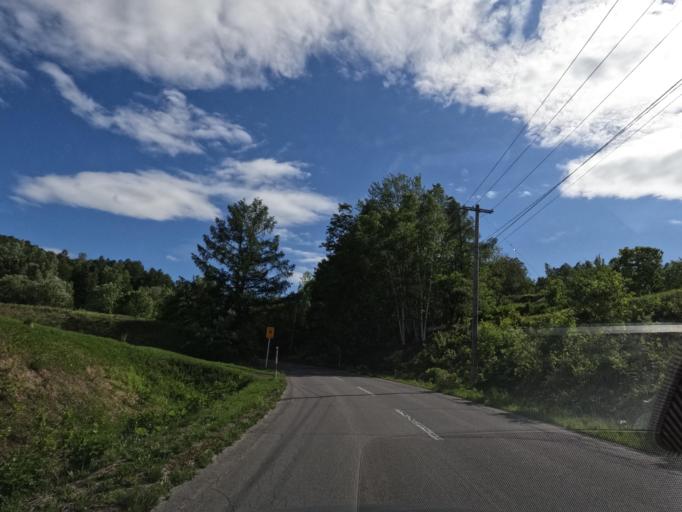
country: JP
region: Hokkaido
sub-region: Asahikawa-shi
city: Asahikawa
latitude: 43.7405
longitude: 142.5336
